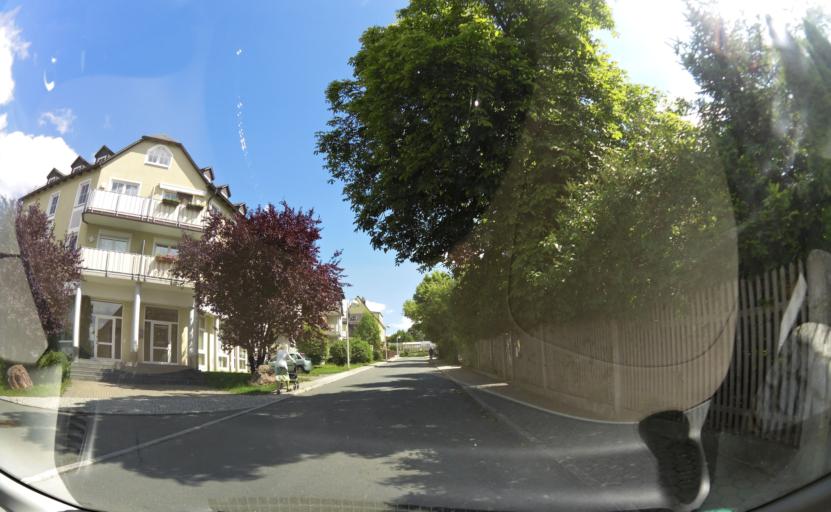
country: DE
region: Thuringia
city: Schleiz
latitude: 50.5796
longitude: 11.8184
